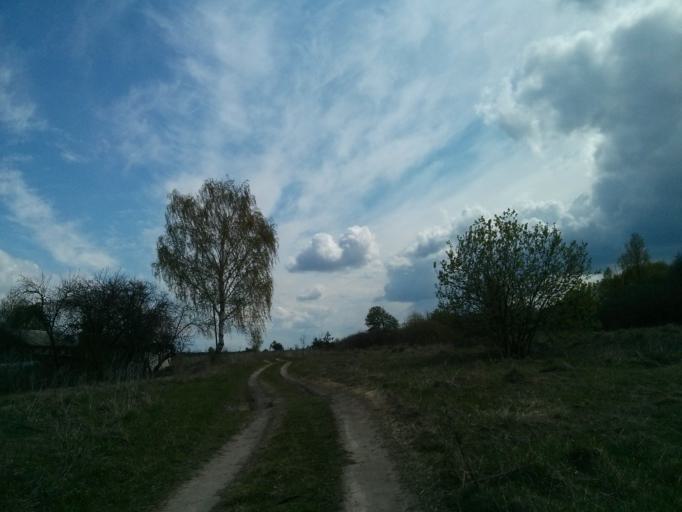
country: RU
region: Nizjnij Novgorod
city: Shimorskoye
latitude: 55.3036
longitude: 41.8458
